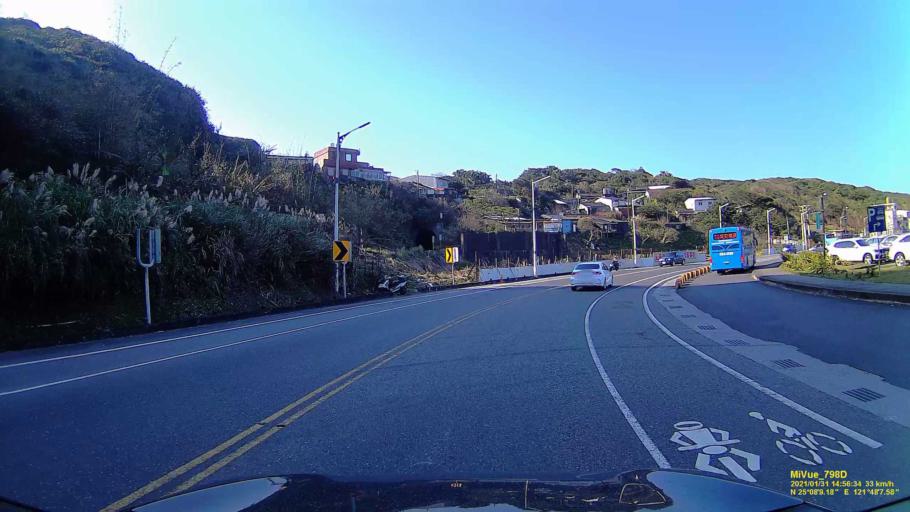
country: TW
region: Taiwan
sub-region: Keelung
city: Keelung
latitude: 25.1360
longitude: 121.8020
